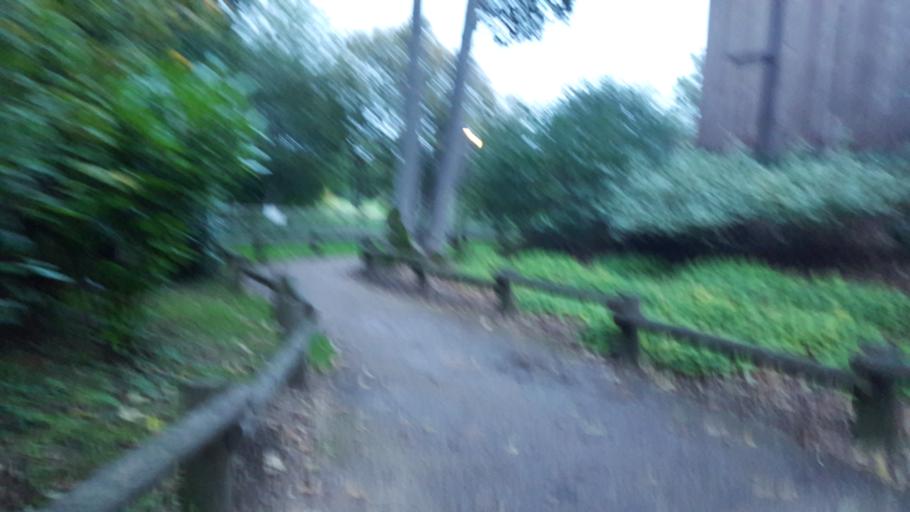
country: GB
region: England
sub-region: Norfolk
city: Weeting
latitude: 52.3934
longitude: 0.6559
